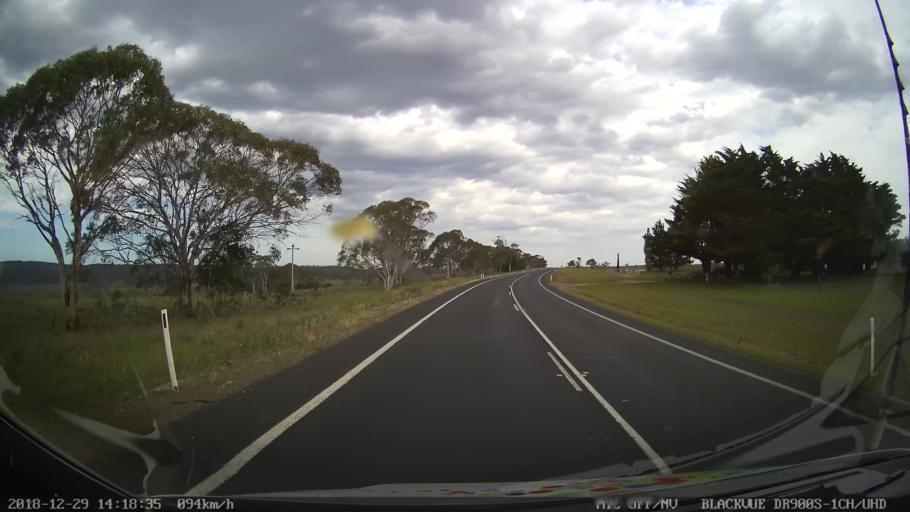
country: AU
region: New South Wales
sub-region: Cooma-Monaro
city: Cooma
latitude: -36.4894
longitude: 149.2713
